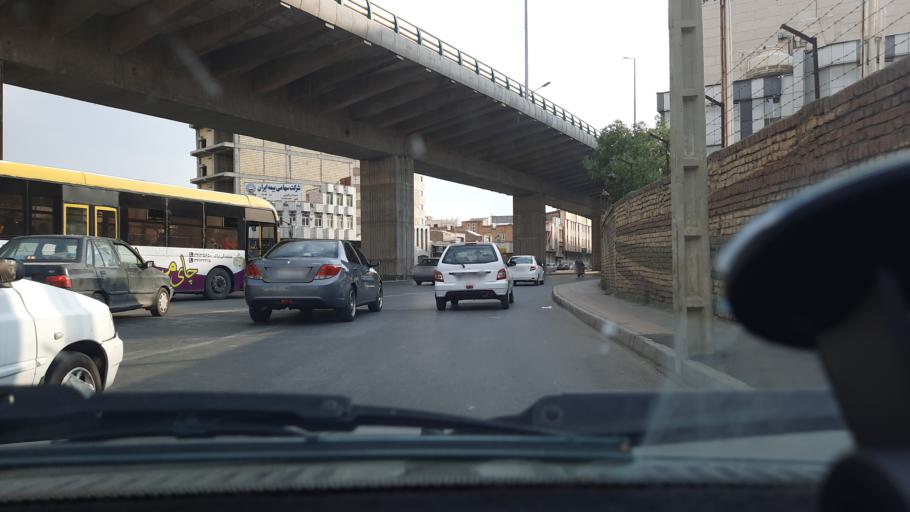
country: IR
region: Markazi
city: Arak
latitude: 34.0778
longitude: 49.6761
